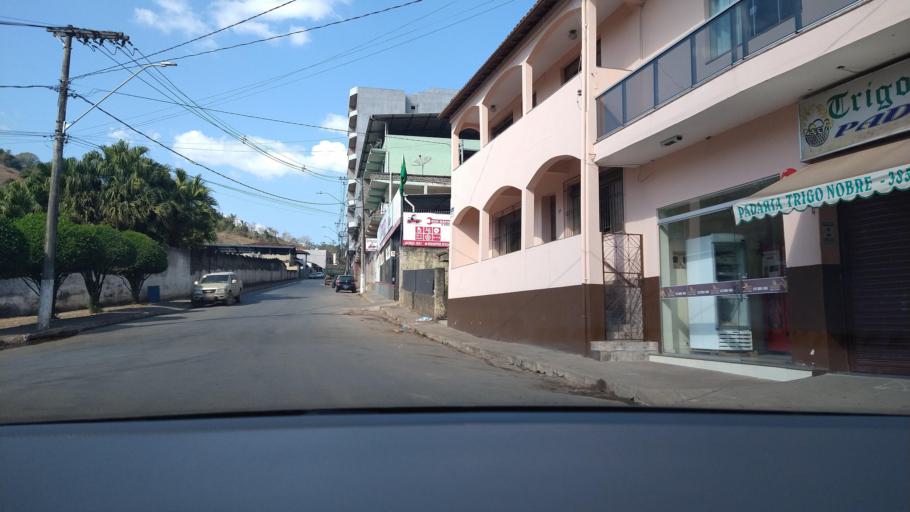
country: BR
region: Minas Gerais
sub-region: Alvinopolis
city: Alvinopolis
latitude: -20.1077
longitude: -43.0575
